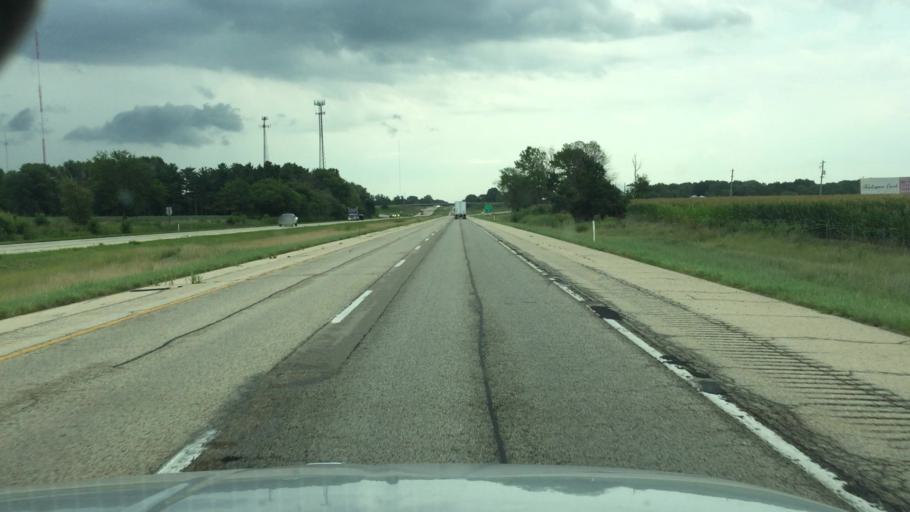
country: US
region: Illinois
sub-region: Peoria County
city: Hanna City
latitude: 40.7779
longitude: -89.7627
